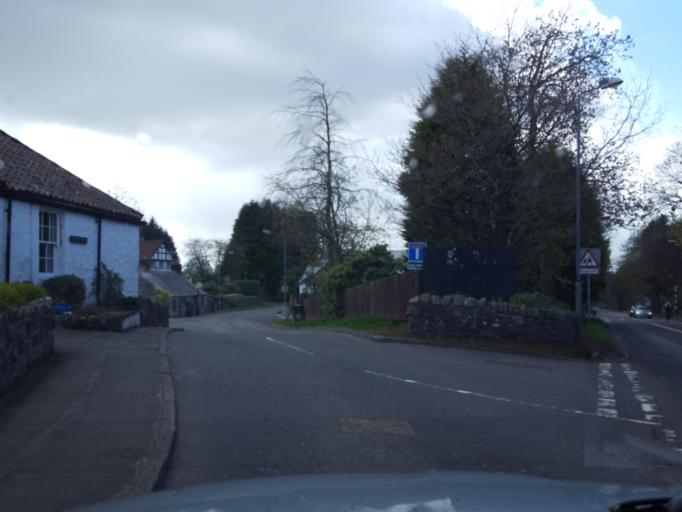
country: GB
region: Scotland
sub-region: Clackmannanshire
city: Dollar
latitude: 56.1879
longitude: -3.6131
